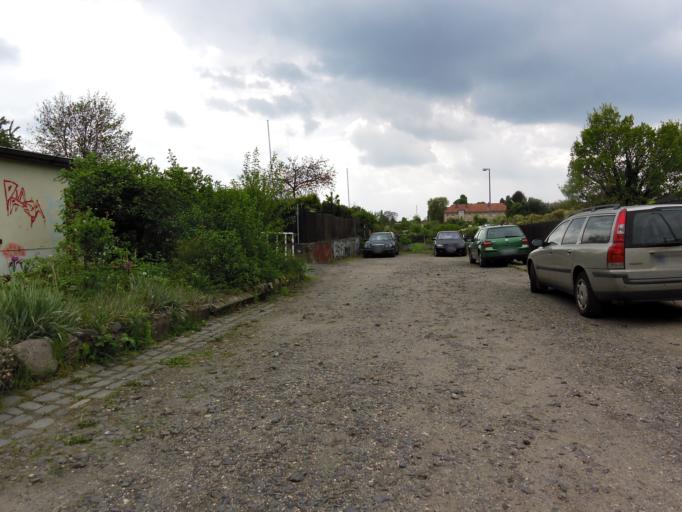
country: DE
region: Saxony
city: Markkleeberg
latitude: 51.3064
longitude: 12.3887
